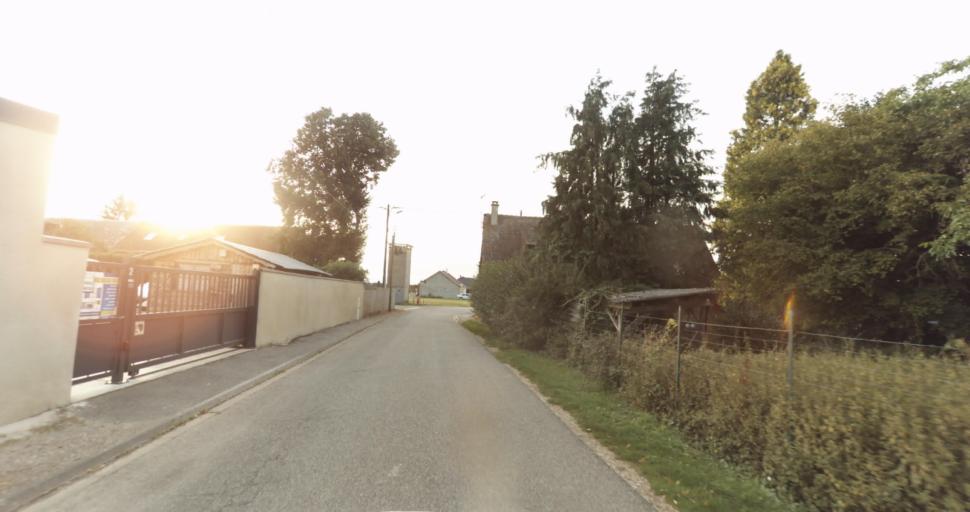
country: FR
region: Haute-Normandie
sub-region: Departement de l'Eure
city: La Madeleine-de-Nonancourt
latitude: 48.8808
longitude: 1.2394
